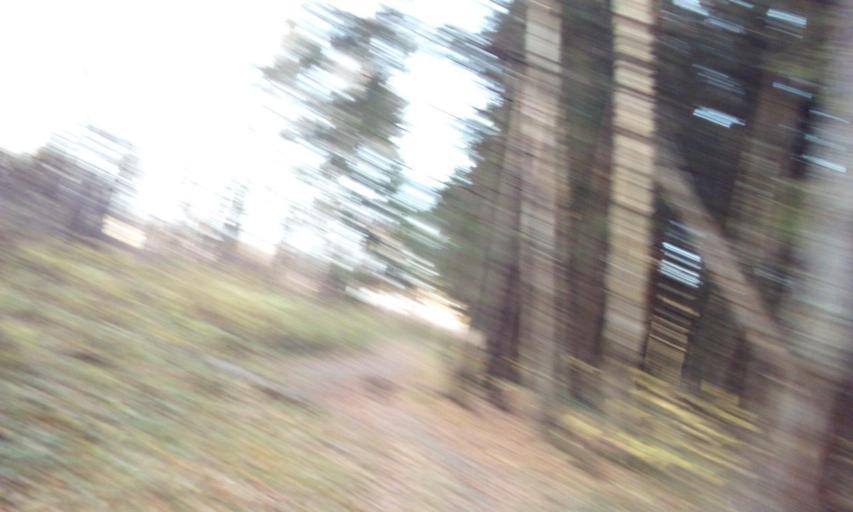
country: RU
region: Moskovskaya
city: Aprelevka
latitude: 55.5568
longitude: 37.1008
